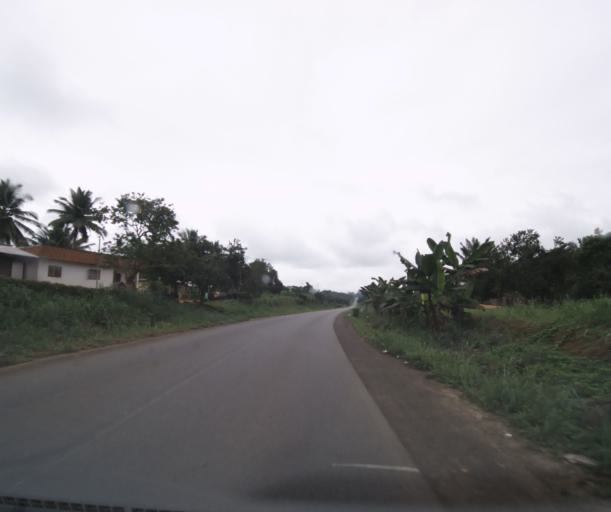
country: CM
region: Littoral
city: Edea
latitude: 3.7105
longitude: 10.1083
